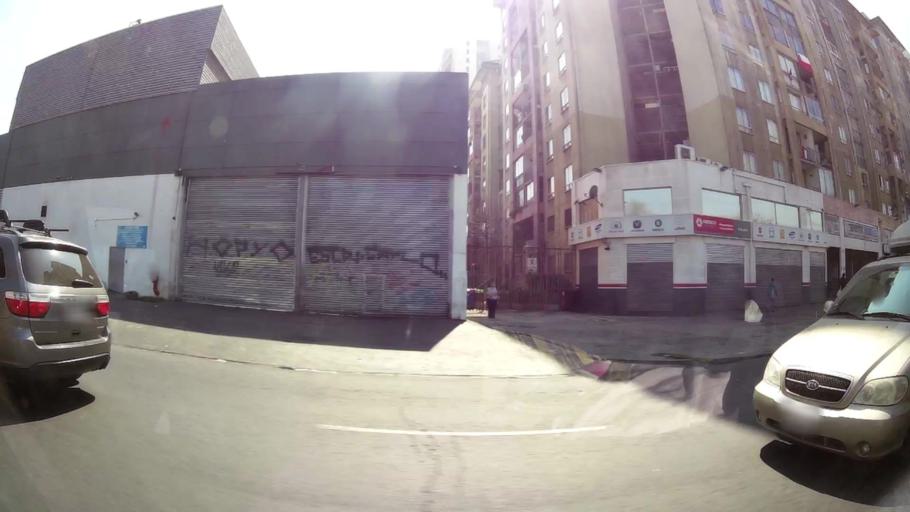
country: CL
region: Santiago Metropolitan
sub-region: Provincia de Santiago
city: Santiago
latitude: -33.4544
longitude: -70.6516
